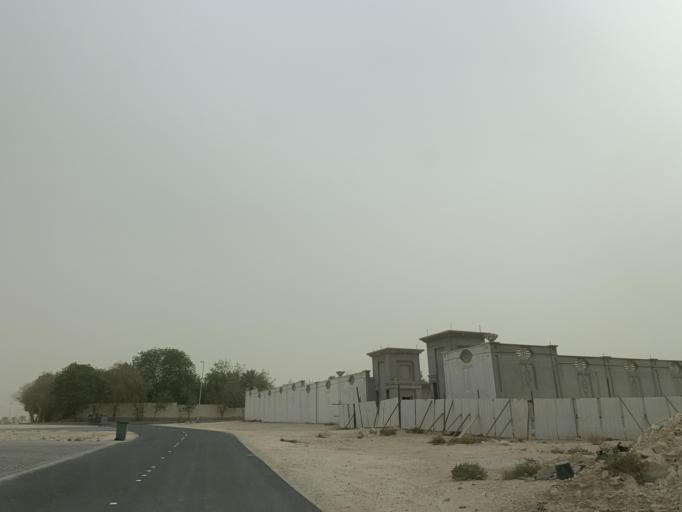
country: BH
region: Northern
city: Ar Rifa'
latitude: 26.1432
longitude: 50.5385
